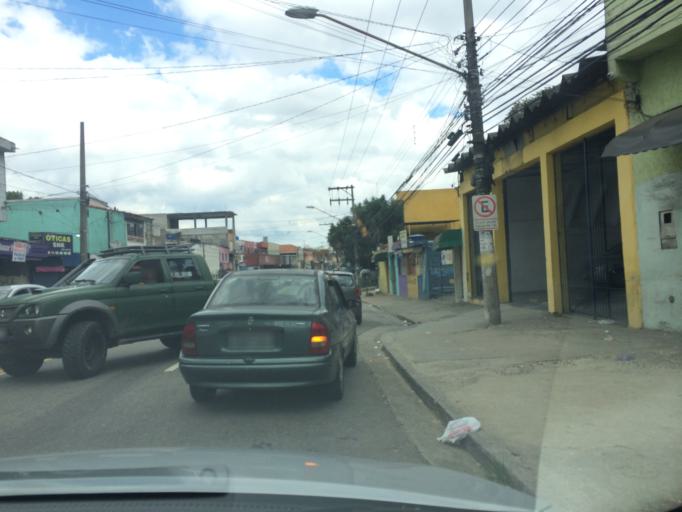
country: BR
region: Sao Paulo
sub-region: Guarulhos
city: Guarulhos
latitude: -23.4303
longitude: -46.5214
